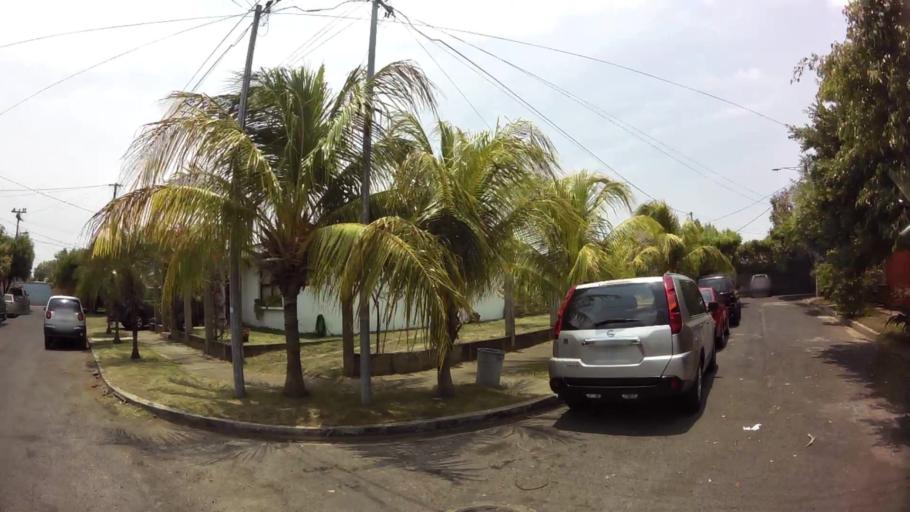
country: NI
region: Managua
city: Managua
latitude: 12.1180
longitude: -86.2885
